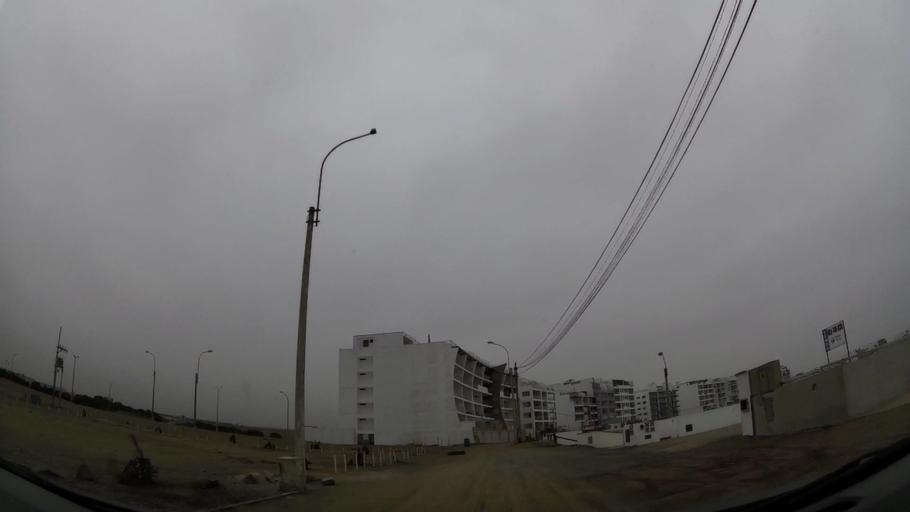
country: PE
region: Lima
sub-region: Lima
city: Punta Hermosa
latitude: -12.3239
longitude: -76.8363
